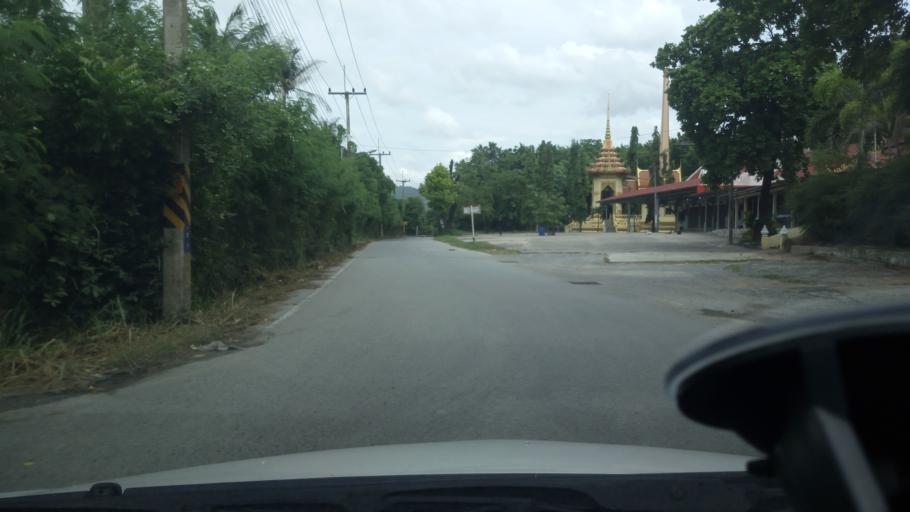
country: TH
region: Chon Buri
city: Chon Buri
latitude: 13.2917
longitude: 100.9684
